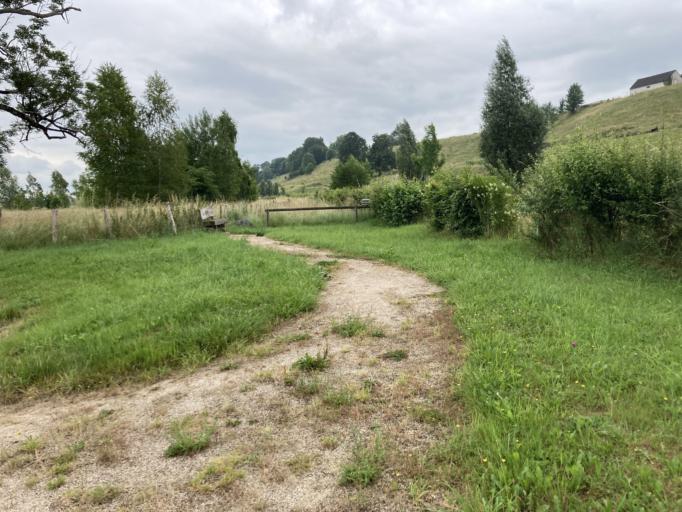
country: FR
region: Aquitaine
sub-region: Departement des Pyrenees-Atlantiques
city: Oloron-Sainte-Marie
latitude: 43.1939
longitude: -0.5989
